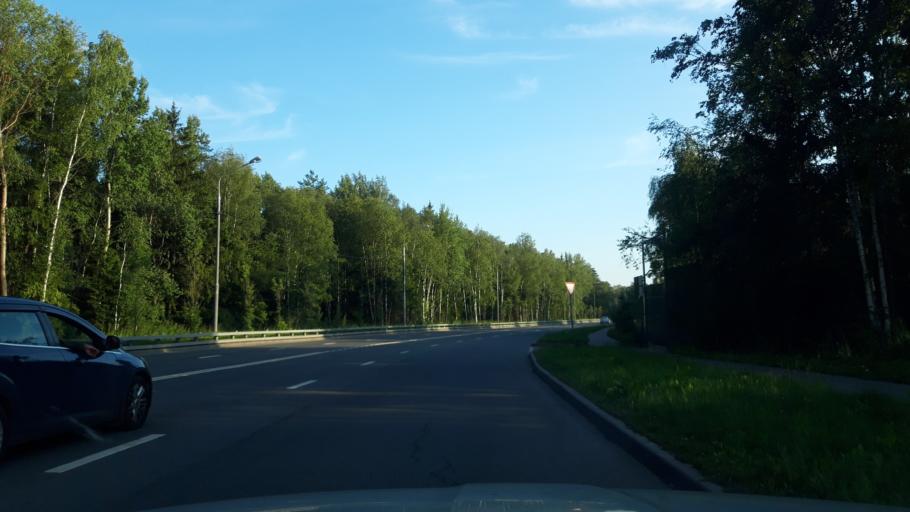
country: RU
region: Moskovskaya
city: Alabushevo
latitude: 56.0055
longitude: 37.1661
